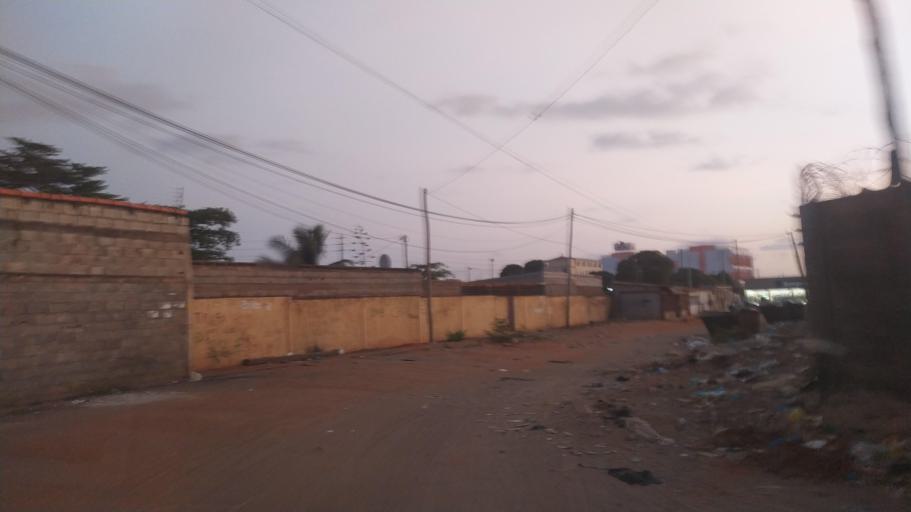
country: AO
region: Luanda
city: Luanda
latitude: -8.8995
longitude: 13.2041
